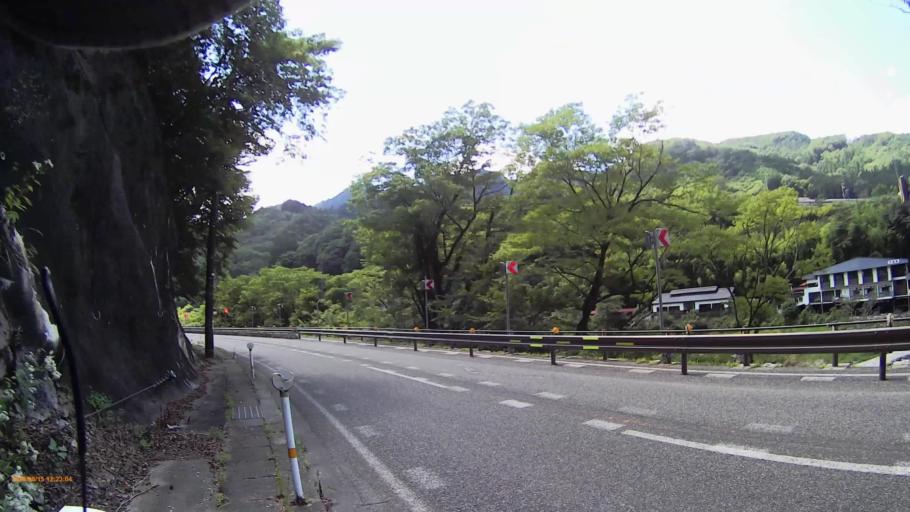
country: JP
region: Nagano
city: Ina
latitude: 35.8062
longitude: 137.6874
